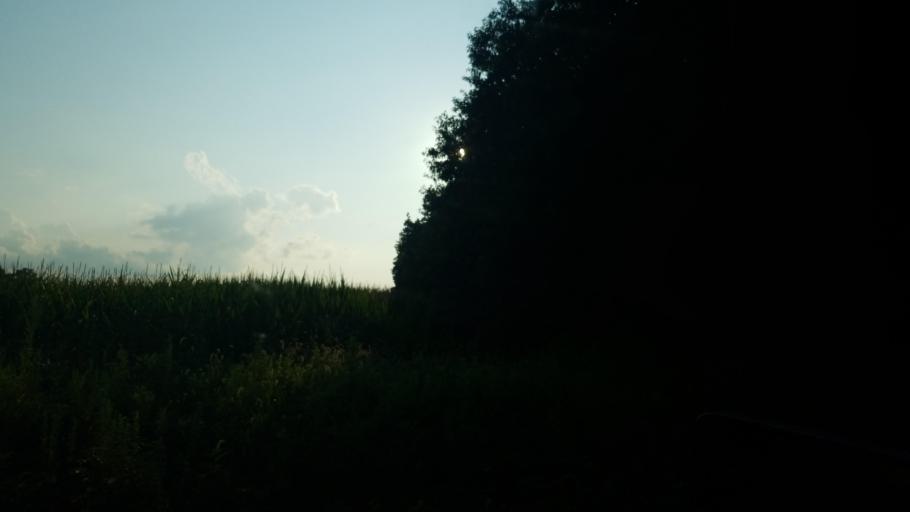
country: US
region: Illinois
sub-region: Saline County
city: Harrisburg
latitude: 37.7920
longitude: -88.6056
